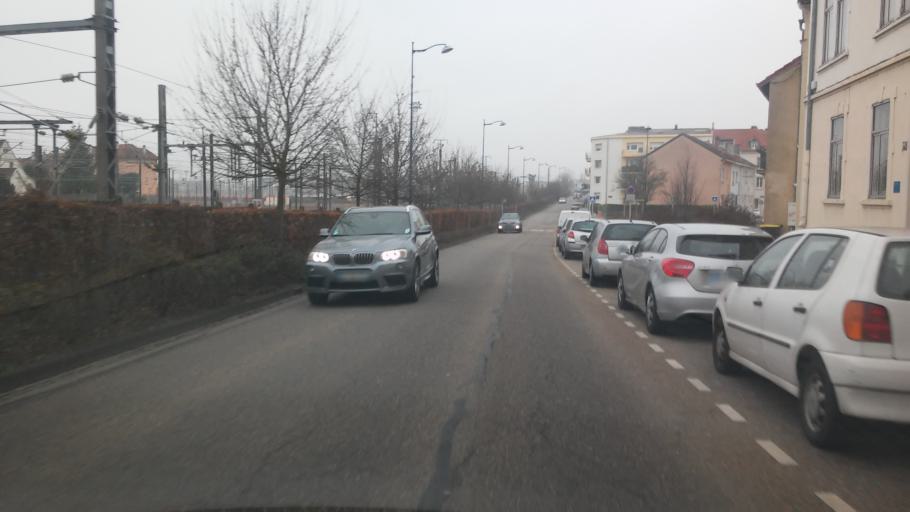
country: FR
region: Lorraine
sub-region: Departement de la Moselle
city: Montigny-les-Metz
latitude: 49.0939
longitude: 6.1739
